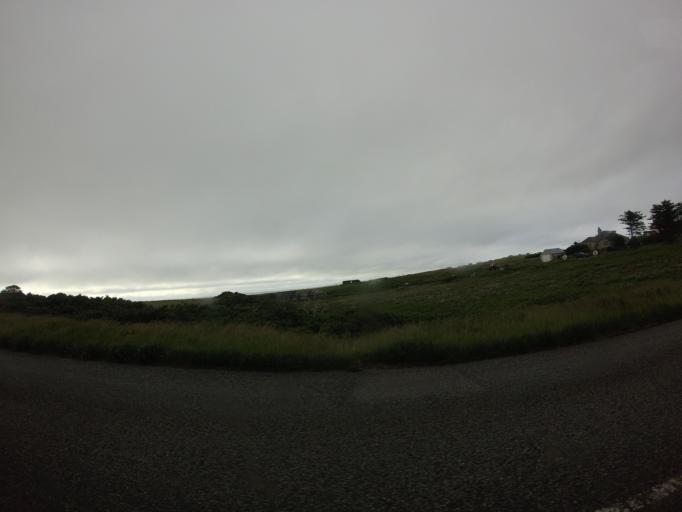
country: GB
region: Scotland
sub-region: Eilean Siar
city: Stornoway
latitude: 58.2091
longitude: -6.2522
